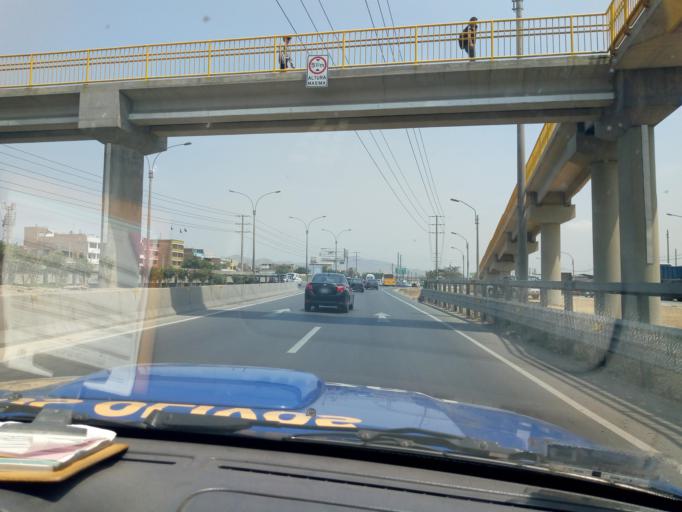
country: PE
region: Lima
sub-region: Lima
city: Independencia
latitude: -11.9746
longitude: -77.0662
